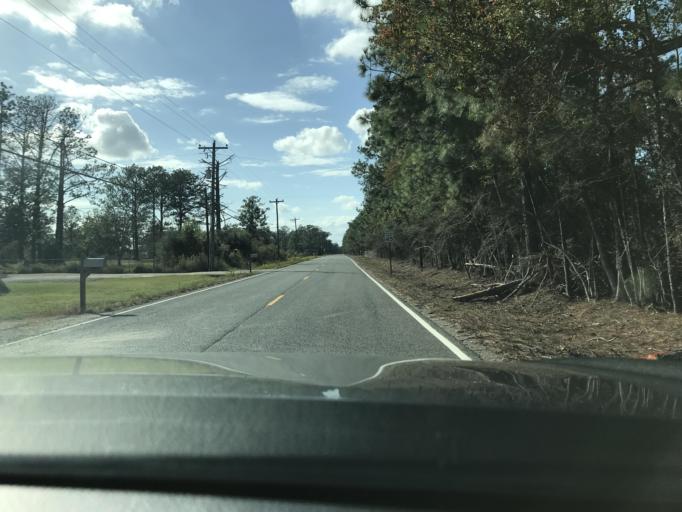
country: US
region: Louisiana
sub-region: Calcasieu Parish
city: Westlake
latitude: 30.3225
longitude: -93.2736
